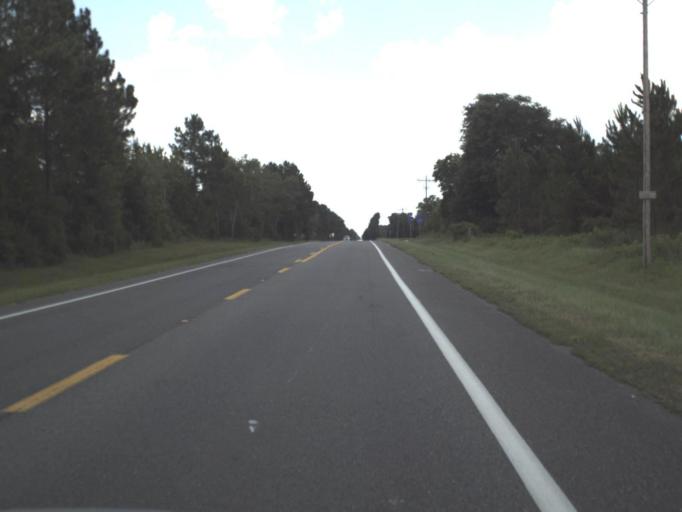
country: US
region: Florida
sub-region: Union County
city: Lake Butler
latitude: 29.9787
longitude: -82.3961
